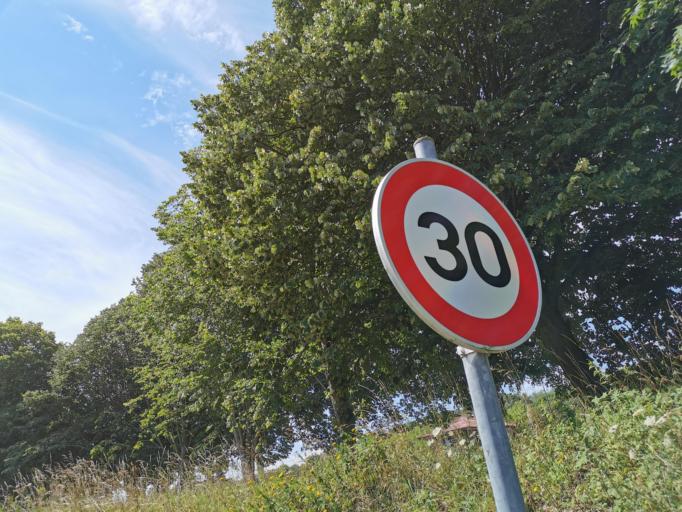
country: BE
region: Wallonia
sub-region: Province du Brabant Wallon
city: Ittre
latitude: 50.6526
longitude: 4.2330
